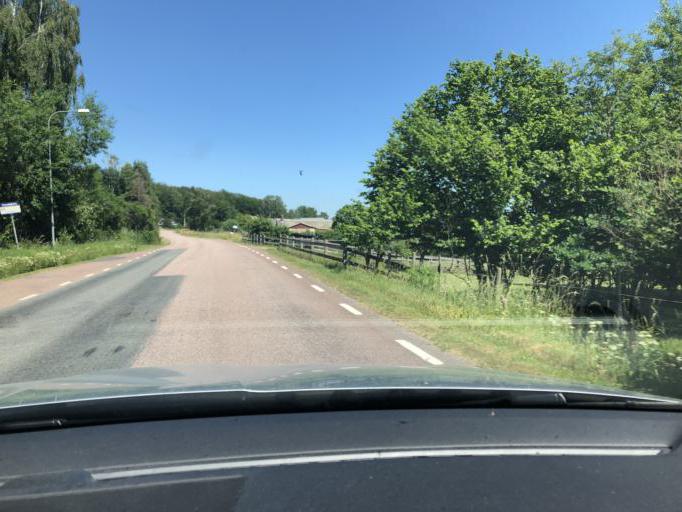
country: SE
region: Blekinge
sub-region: Olofstroms Kommun
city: Jamshog
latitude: 56.1651
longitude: 14.5987
